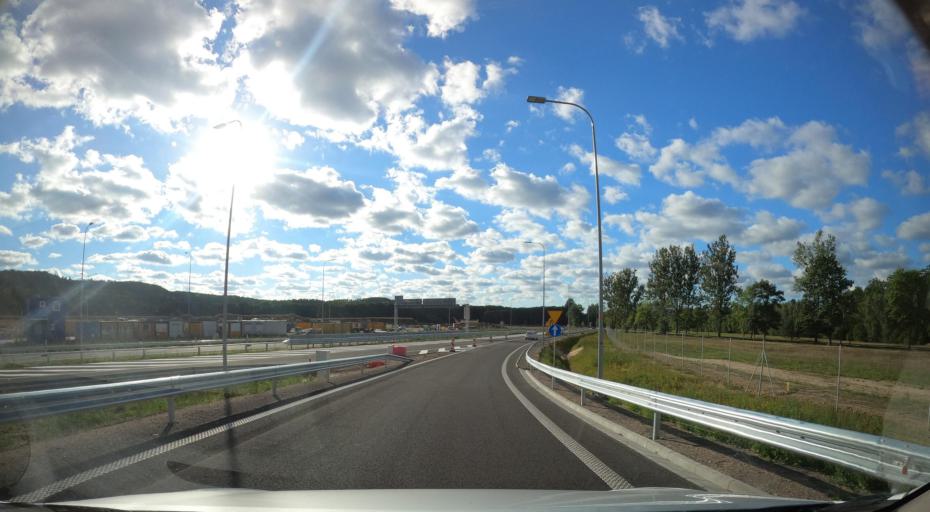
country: PL
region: Pomeranian Voivodeship
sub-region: Powiat wejherowski
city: Leczyce
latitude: 54.5685
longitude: 17.9633
